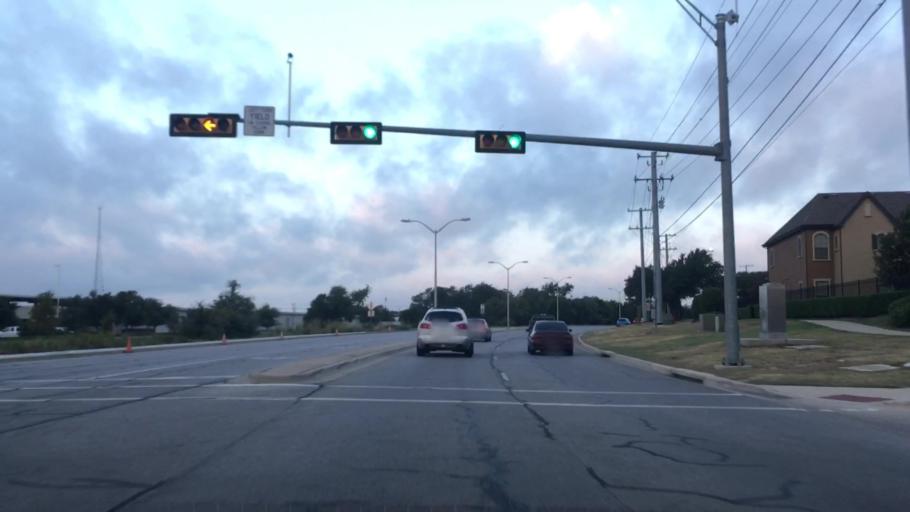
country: US
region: Texas
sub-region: Williamson County
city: Cedar Park
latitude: 30.5035
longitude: -97.8022
